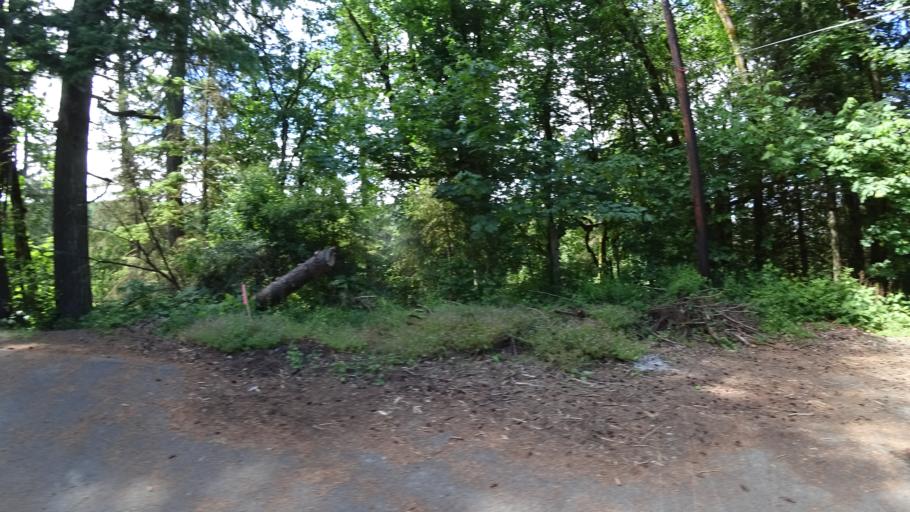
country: US
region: Oregon
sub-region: Washington County
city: Bethany
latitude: 45.6164
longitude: -122.8135
